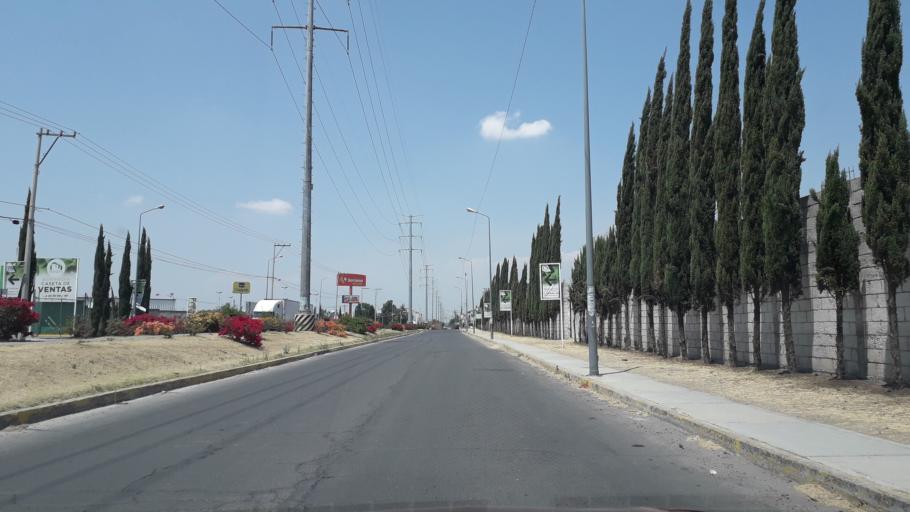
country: MX
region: Puebla
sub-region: Amozoc
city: Casa Blanca
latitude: 19.0618
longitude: -98.1240
